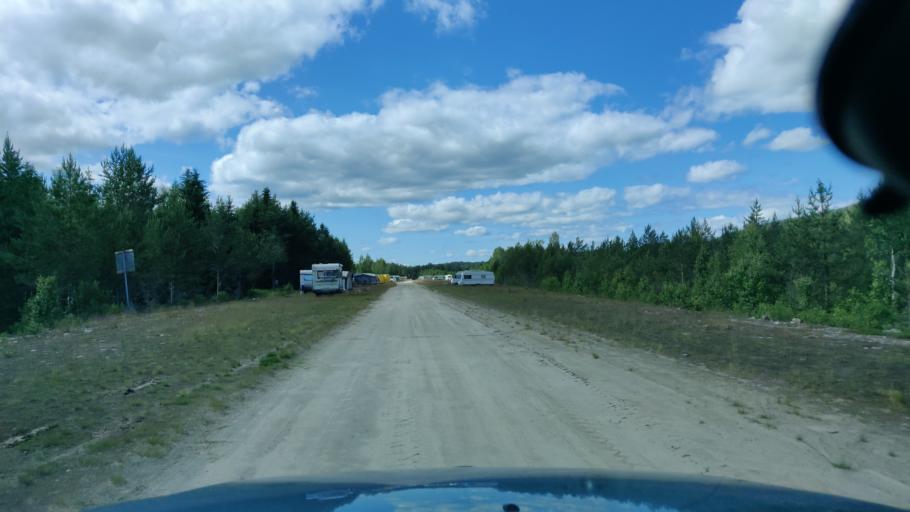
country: NO
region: Hedmark
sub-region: Trysil
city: Innbygda
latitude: 60.9076
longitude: 12.5694
